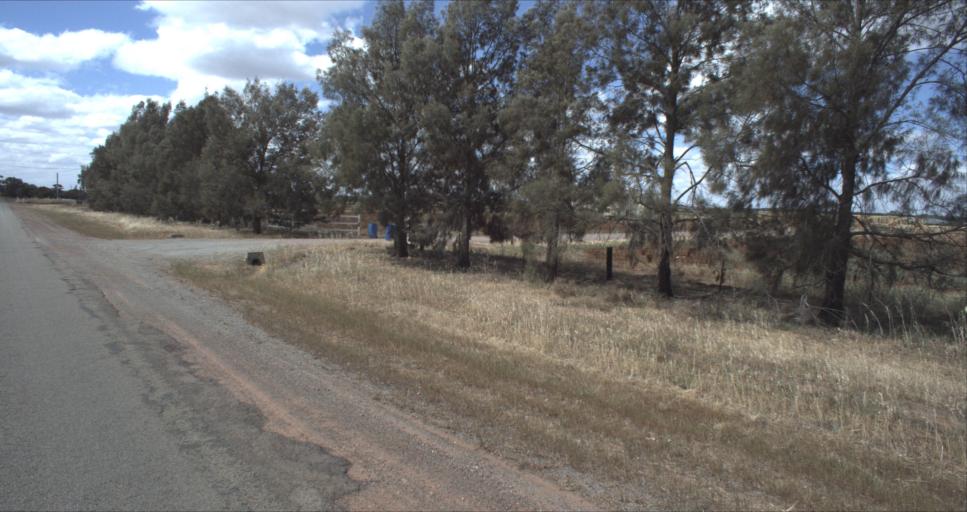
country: AU
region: New South Wales
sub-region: Leeton
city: Leeton
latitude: -34.5853
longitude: 146.3961
